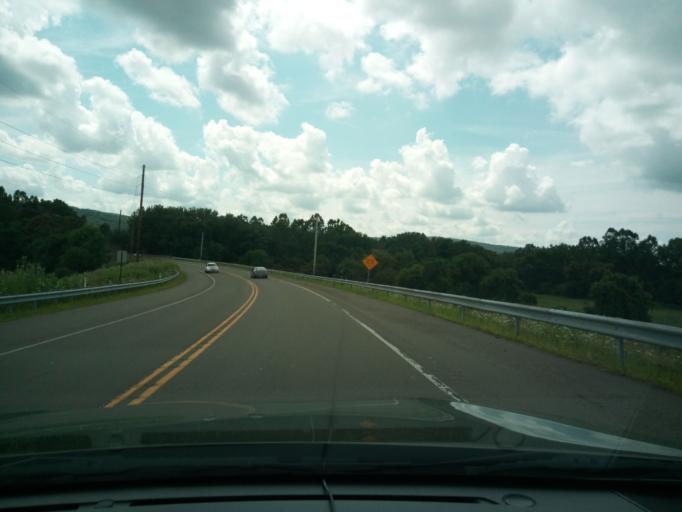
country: US
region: Pennsylvania
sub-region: Bradford County
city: South Waverly
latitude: 41.9886
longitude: -76.5514
